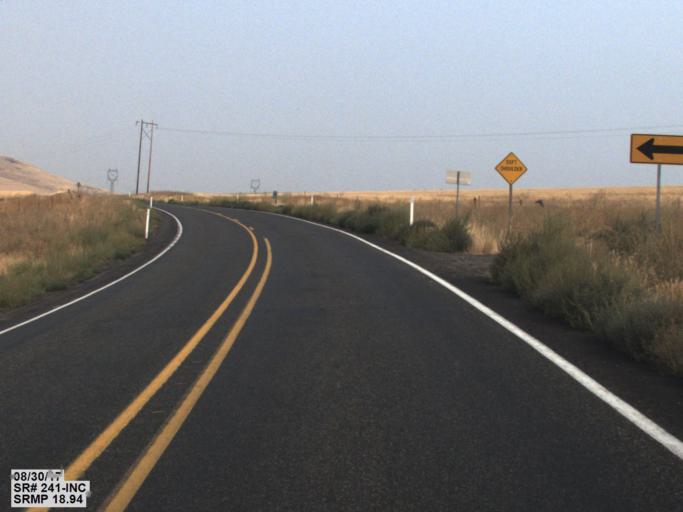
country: US
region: Washington
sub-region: Yakima County
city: Sunnyside
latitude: 46.4634
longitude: -119.9345
